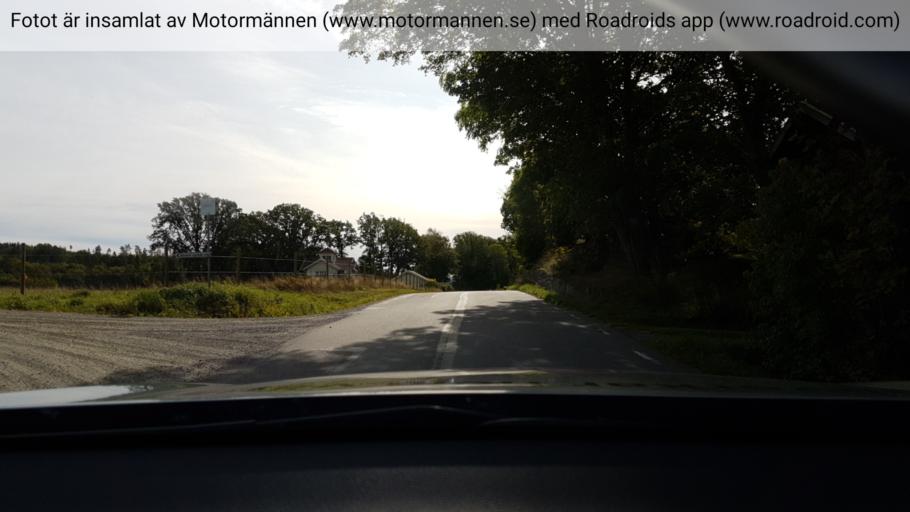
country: SE
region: Vaestra Goetaland
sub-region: Uddevalla Kommun
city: Ljungskile
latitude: 58.2530
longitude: 11.8608
